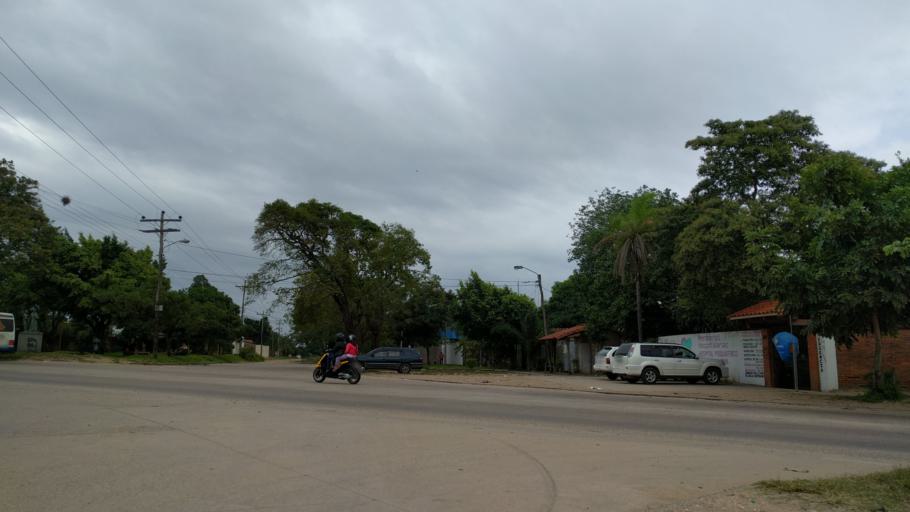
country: BO
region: Santa Cruz
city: Santa Cruz de la Sierra
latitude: -17.8076
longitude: -63.2278
